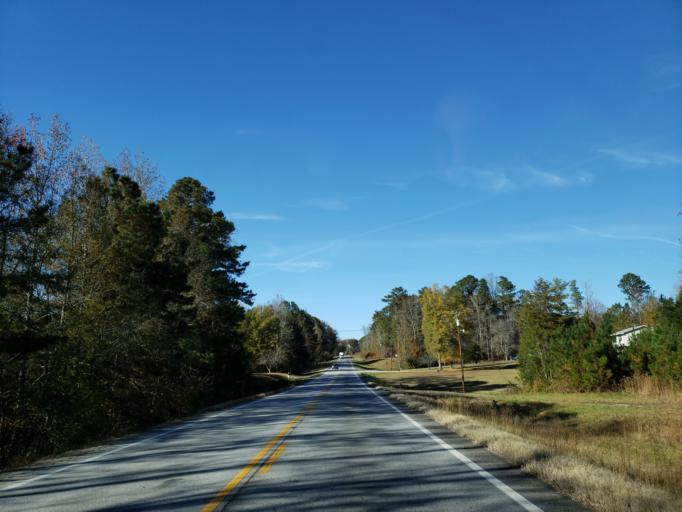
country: US
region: Alabama
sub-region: Calhoun County
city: Choccolocco
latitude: 33.5608
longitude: -85.6617
